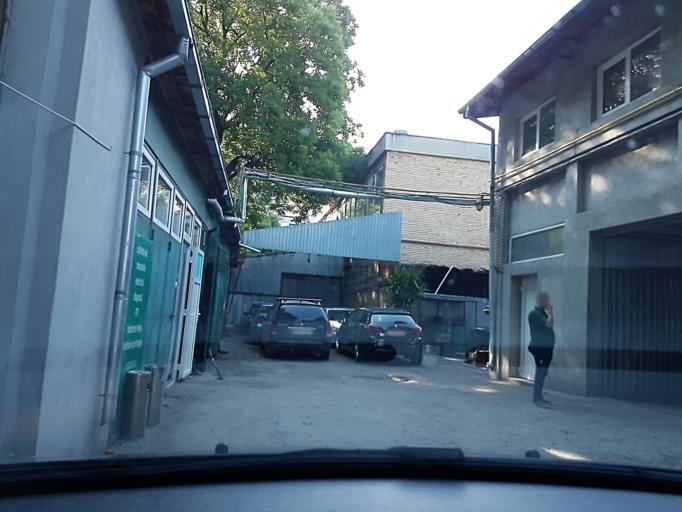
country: RO
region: Bucuresti
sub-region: Municipiul Bucuresti
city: Bucuresti
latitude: 44.3972
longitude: 26.1144
